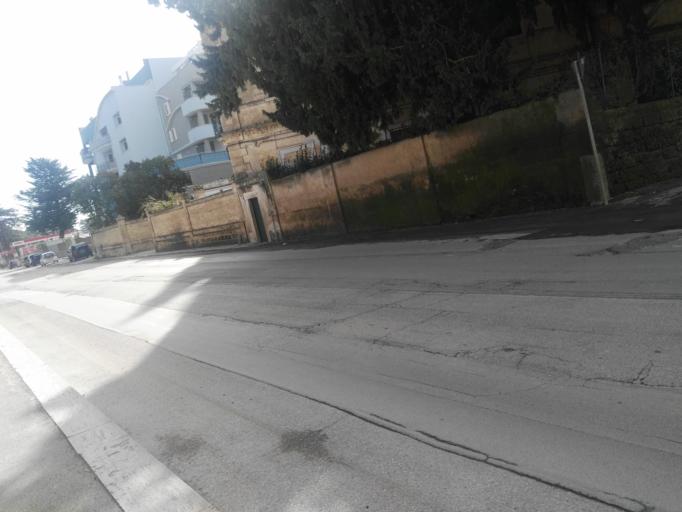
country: IT
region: Apulia
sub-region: Provincia di Barletta - Andria - Trani
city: Andria
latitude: 41.2181
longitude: 16.3082
